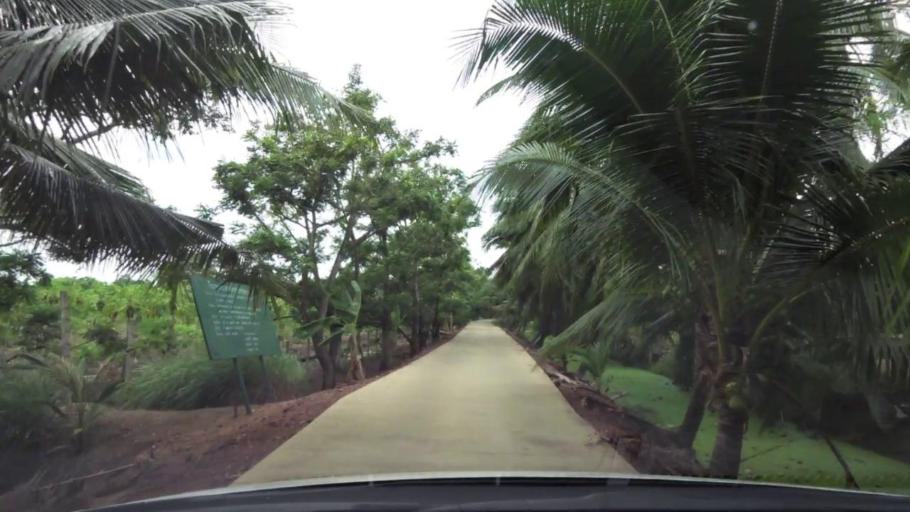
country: TH
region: Ratchaburi
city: Damnoen Saduak
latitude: 13.5549
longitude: 99.9978
